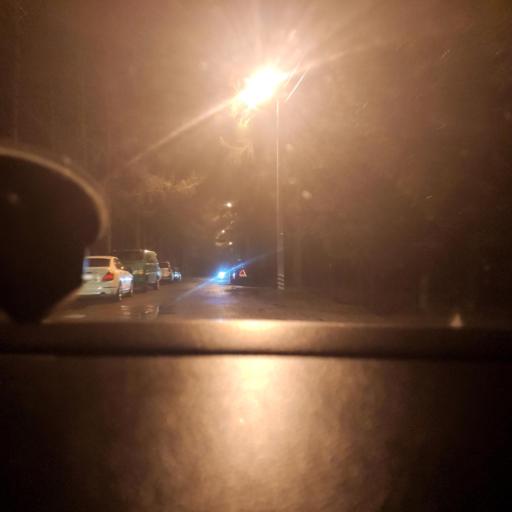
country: RU
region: Moskovskaya
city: Yershovo
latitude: 55.7980
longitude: 36.8527
